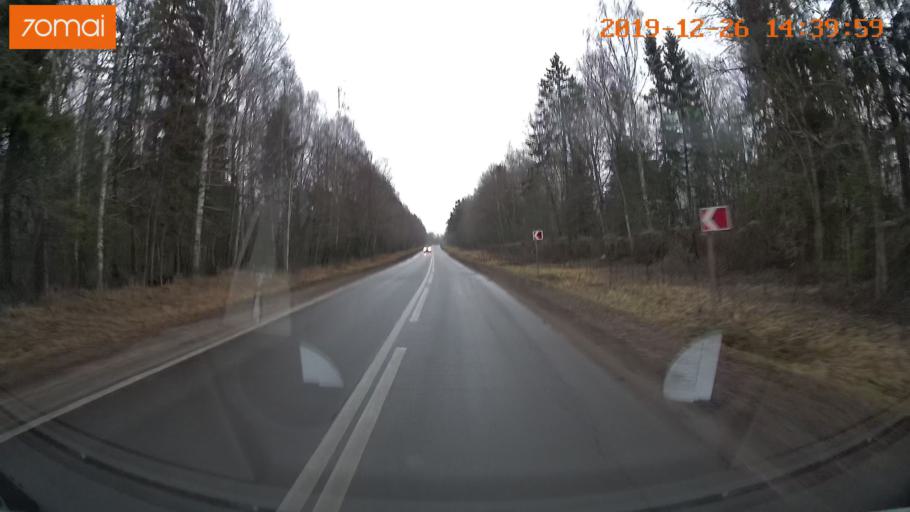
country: RU
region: Jaroslavl
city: Poshekhon'ye
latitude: 58.3787
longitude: 38.9892
